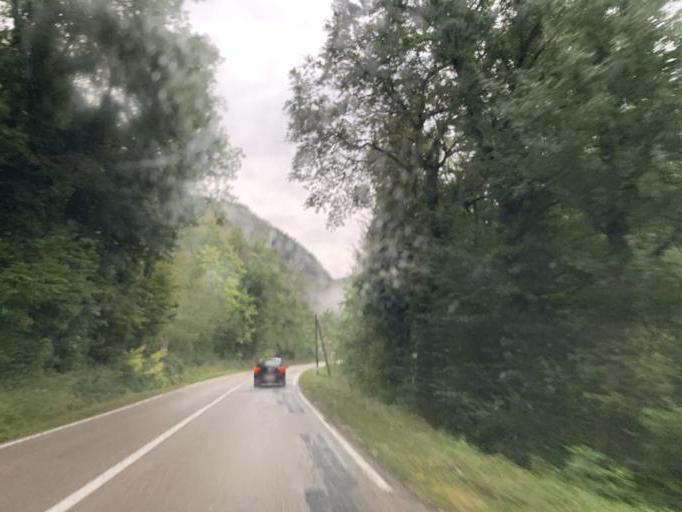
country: FR
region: Rhone-Alpes
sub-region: Departement de l'Isere
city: Les Avenieres
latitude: 45.6751
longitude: 5.6073
